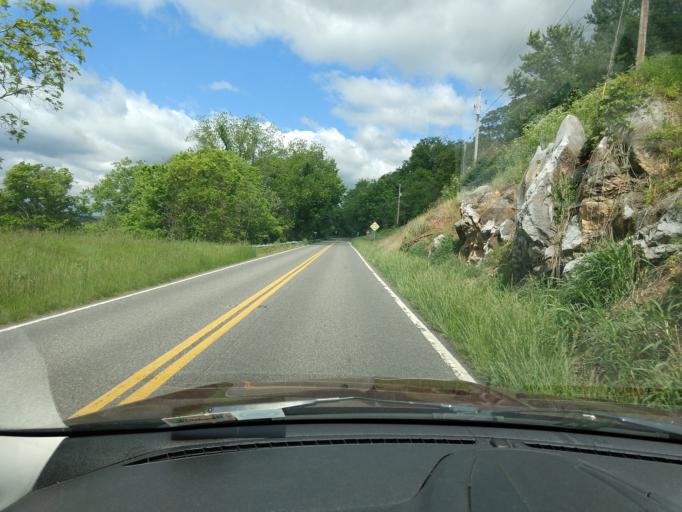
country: US
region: Virginia
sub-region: Wythe County
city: Wytheville
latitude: 36.8391
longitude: -80.9641
